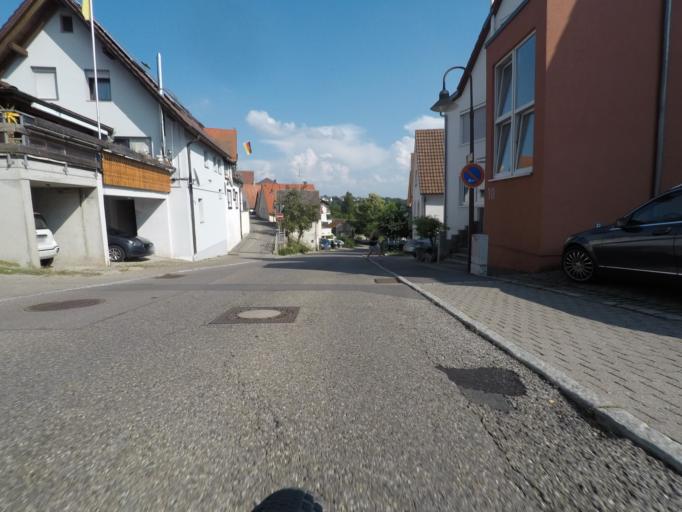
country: DE
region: Baden-Wuerttemberg
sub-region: Regierungsbezirk Stuttgart
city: Weil im Schonbuch
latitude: 48.6212
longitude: 9.0634
